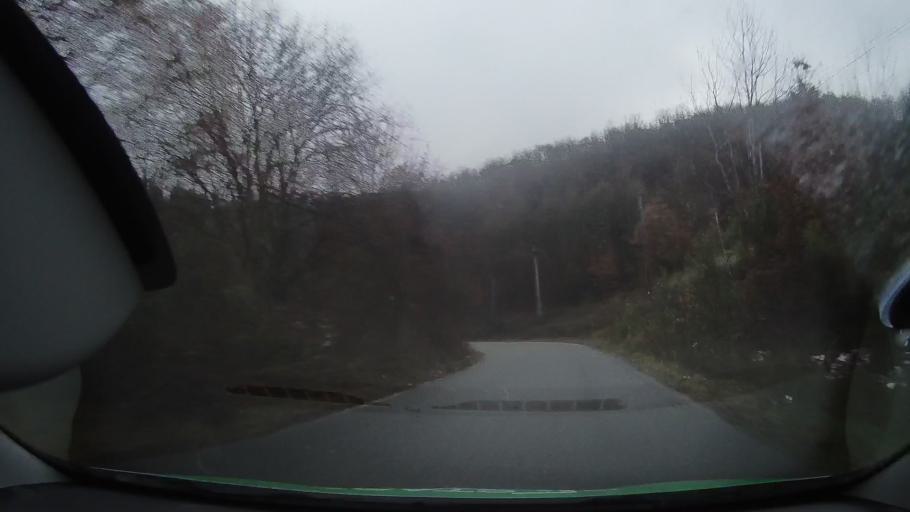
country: RO
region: Hunedoara
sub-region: Comuna Ribita
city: Ribita
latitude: 46.2348
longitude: 22.7460
